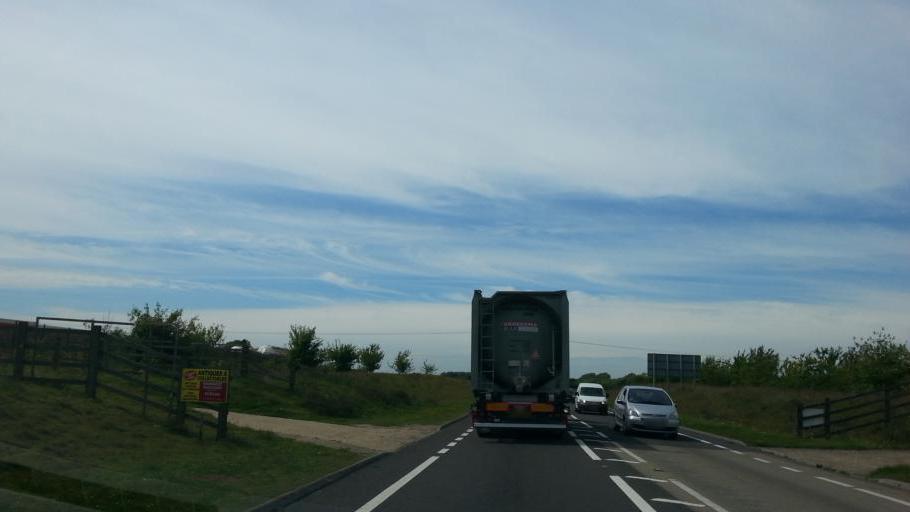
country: GB
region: England
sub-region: Suffolk
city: Exning
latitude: 52.2949
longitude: 0.3879
